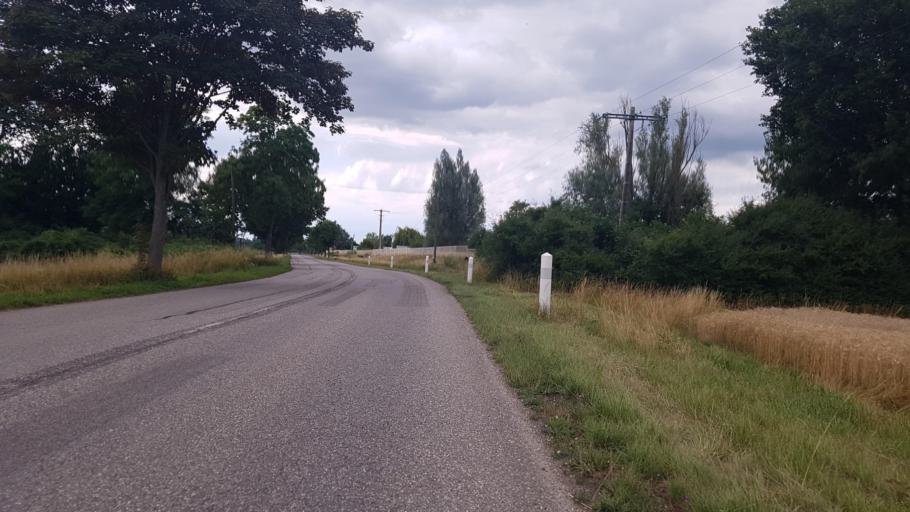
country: FR
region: Alsace
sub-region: Departement du Bas-Rhin
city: Gambsheim
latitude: 48.7034
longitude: 7.8703
